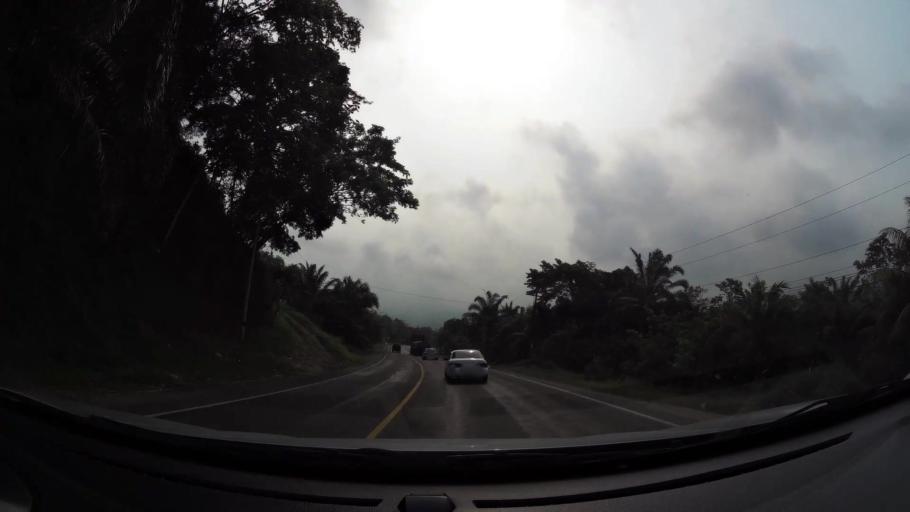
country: HN
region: Yoro
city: Toyos
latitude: 15.5540
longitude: -87.6390
